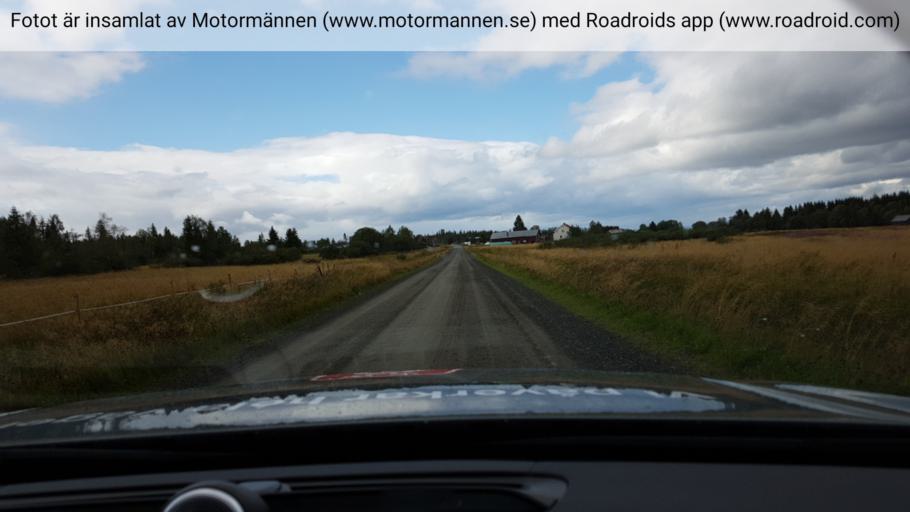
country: SE
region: Jaemtland
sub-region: OEstersunds Kommun
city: Lit
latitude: 63.6798
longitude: 14.8613
